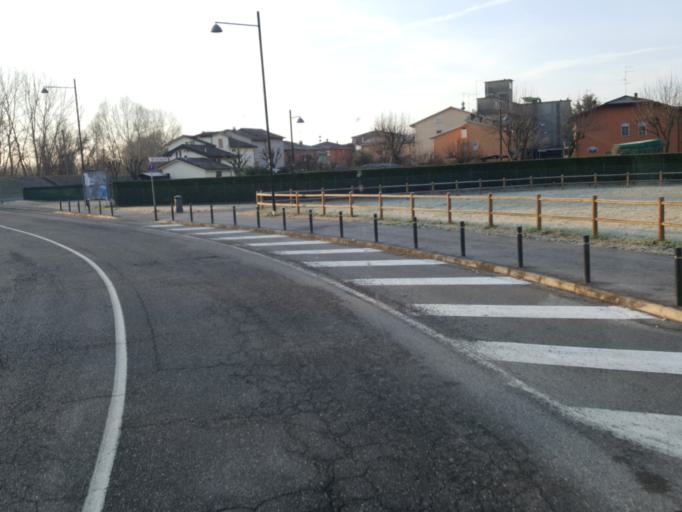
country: IT
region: Emilia-Romagna
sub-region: Provincia di Parma
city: Sorbolo
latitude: 44.8481
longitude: 10.4518
